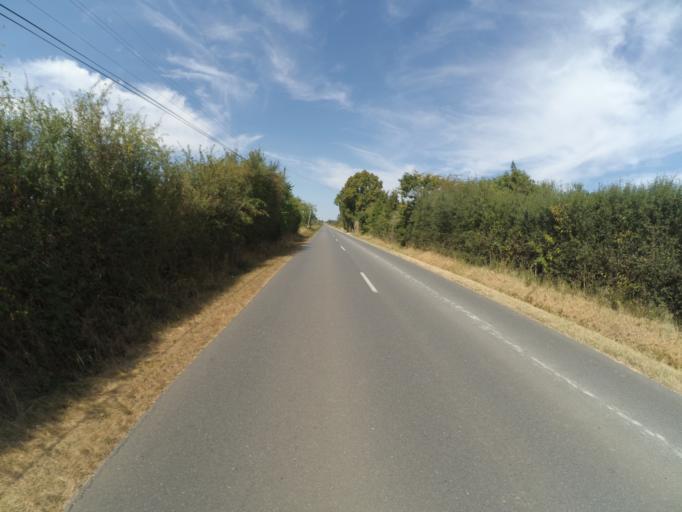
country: FR
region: Poitou-Charentes
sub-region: Departement de la Vienne
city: Availles-Limouzine
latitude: 46.1567
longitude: 0.5515
